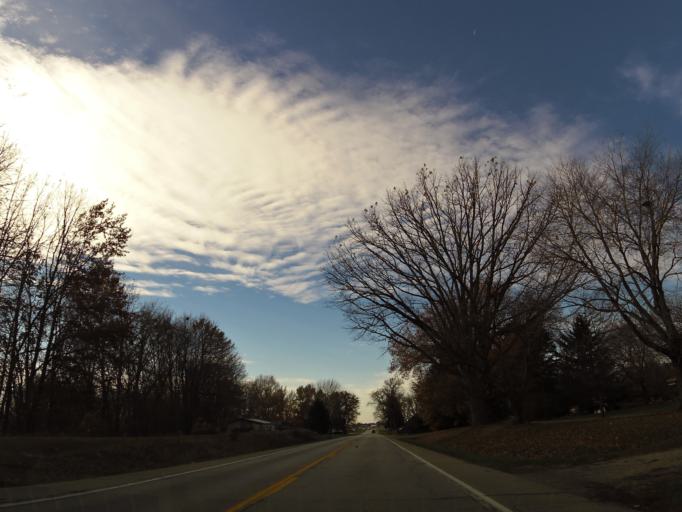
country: US
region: Illinois
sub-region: De Witt County
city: Farmer City
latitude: 40.2475
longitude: -88.6278
